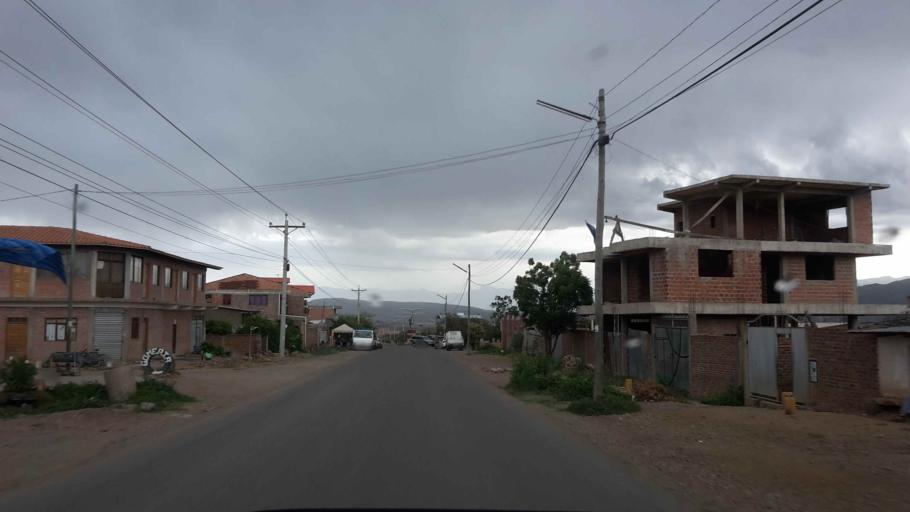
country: BO
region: Cochabamba
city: Tarata
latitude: -17.6063
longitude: -66.0298
